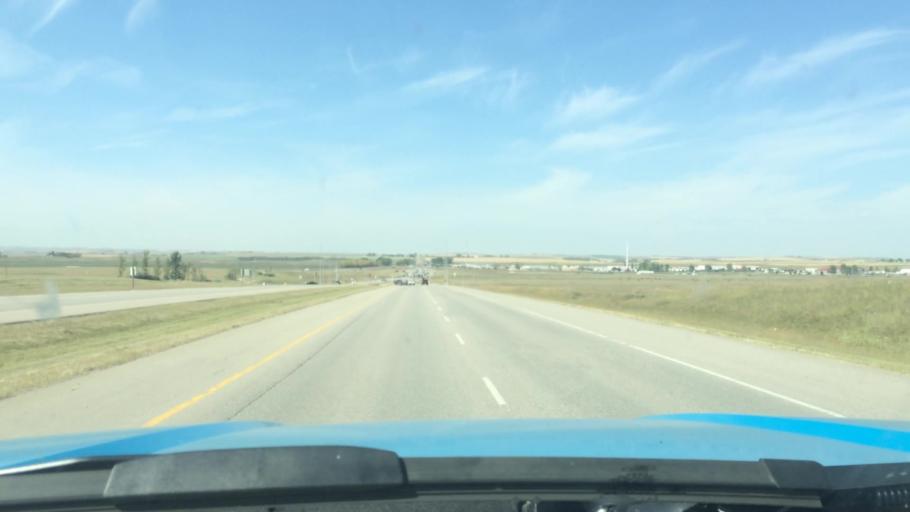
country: CA
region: Alberta
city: Airdrie
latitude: 51.2125
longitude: -113.9851
